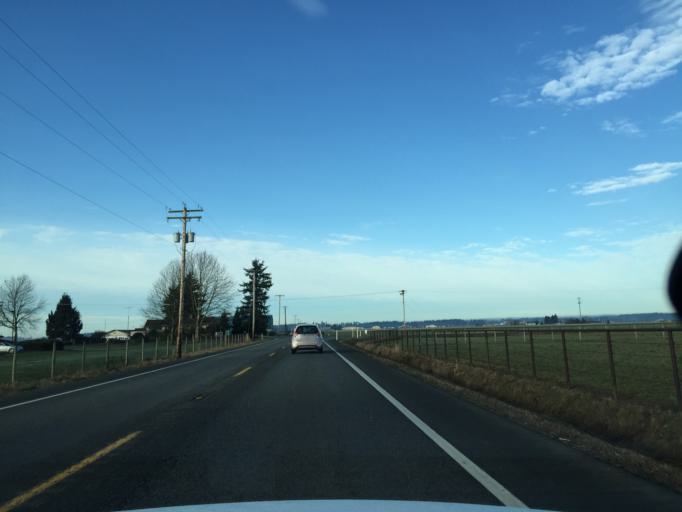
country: US
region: Washington
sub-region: Whatcom County
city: Lynden
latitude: 48.9647
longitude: -122.4612
